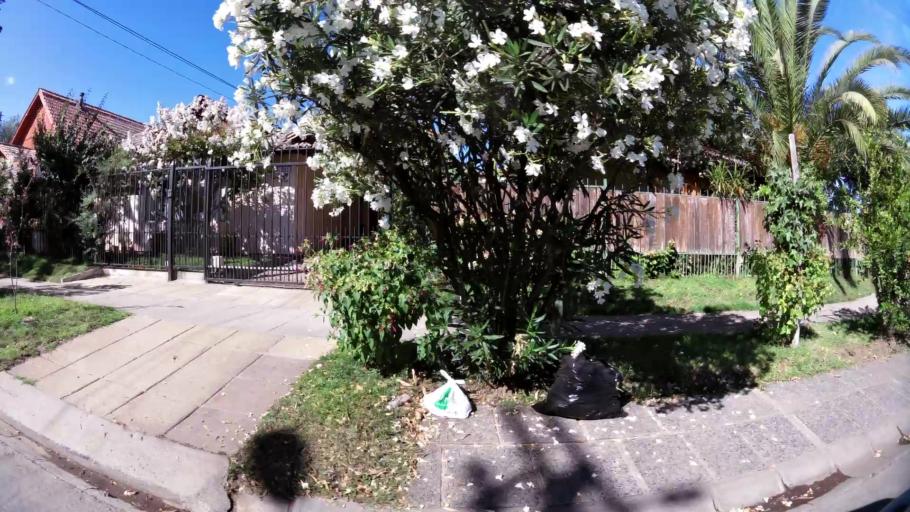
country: CL
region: O'Higgins
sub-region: Provincia de Cachapoal
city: Rancagua
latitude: -34.1823
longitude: -70.7083
